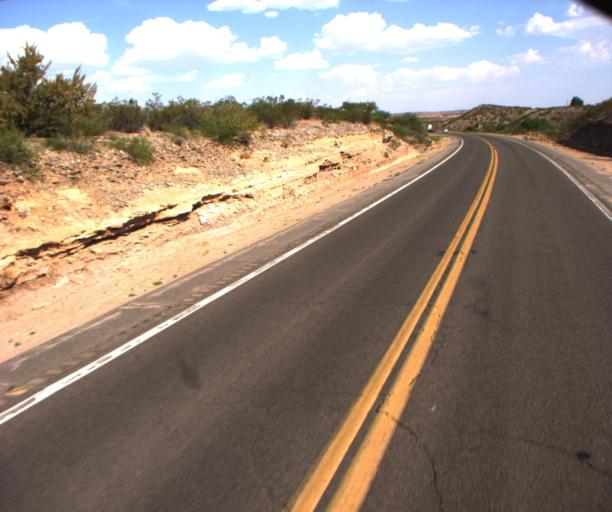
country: US
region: Arizona
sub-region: Greenlee County
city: Clifton
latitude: 32.8009
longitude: -109.1664
